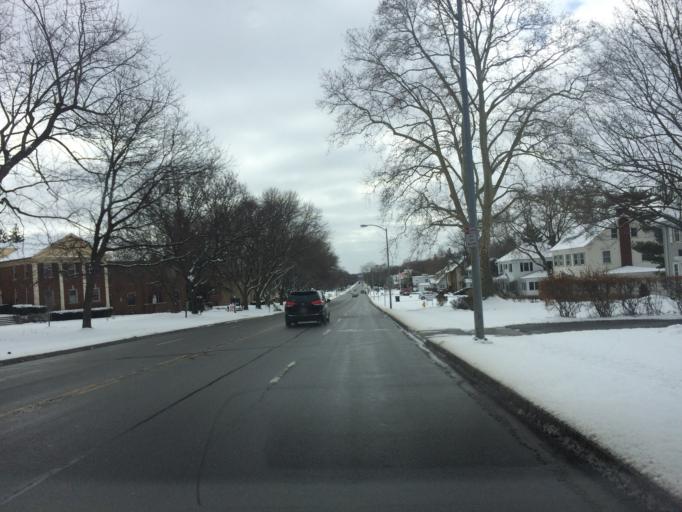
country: US
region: New York
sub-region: Monroe County
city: Brighton
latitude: 43.1357
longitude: -77.5750
